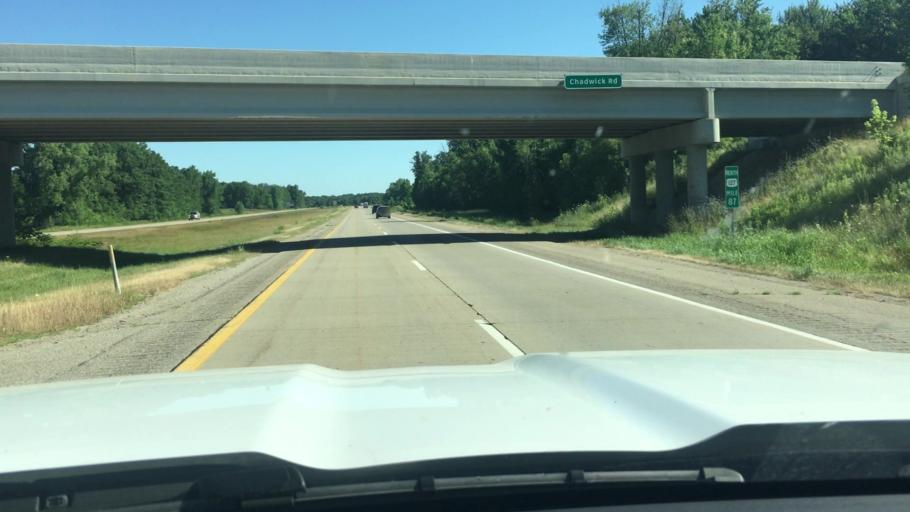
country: US
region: Michigan
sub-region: Clinton County
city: DeWitt
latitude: 42.8707
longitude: -84.5180
